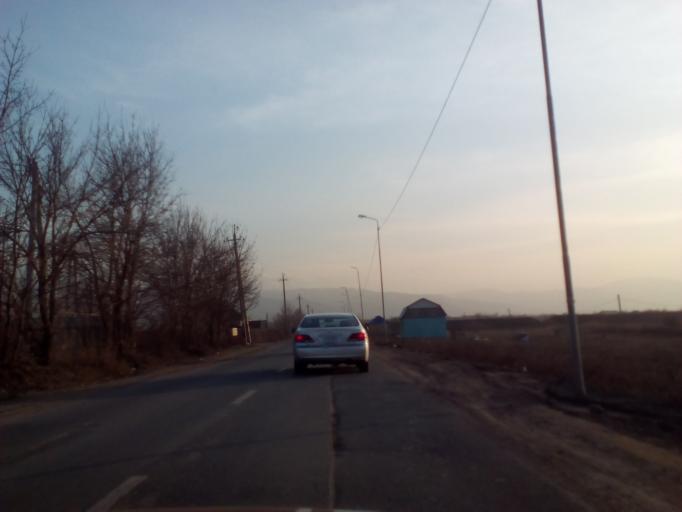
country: KZ
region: Almaty Oblysy
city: Burunday
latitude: 43.2365
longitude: 76.7425
